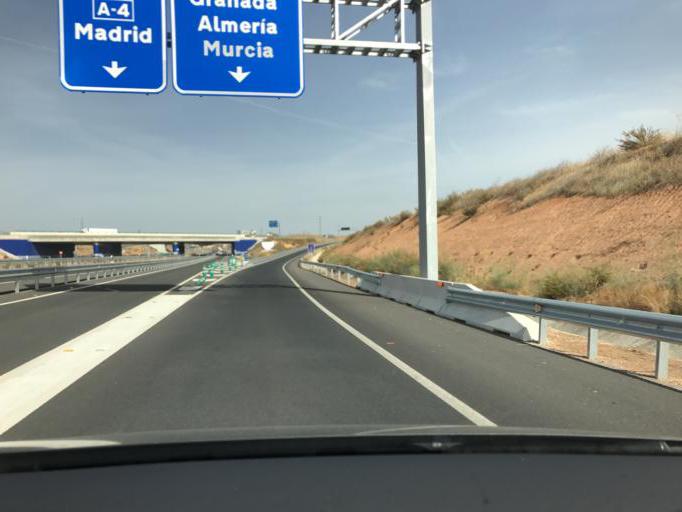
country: ES
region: Andalusia
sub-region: Provincia de Granada
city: Albolote
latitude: 37.2311
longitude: -3.6653
